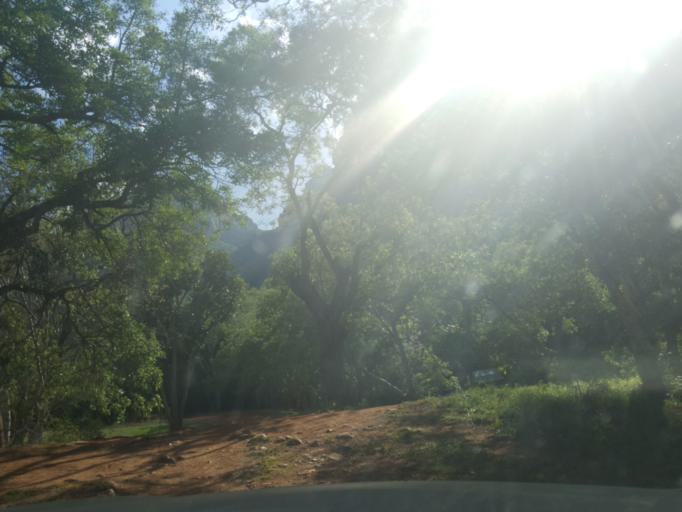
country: ZA
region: Limpopo
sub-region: Mopani District Municipality
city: Hoedspruit
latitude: -24.5930
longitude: 30.8248
